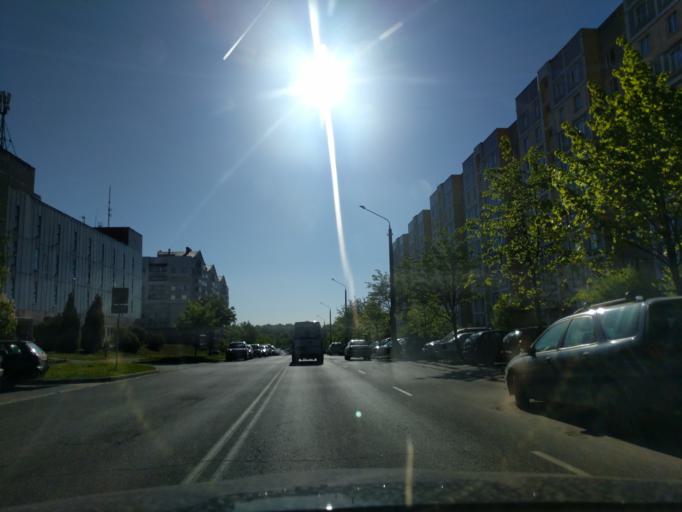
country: BY
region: Minsk
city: Novoye Medvezhino
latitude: 53.9041
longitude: 27.4585
